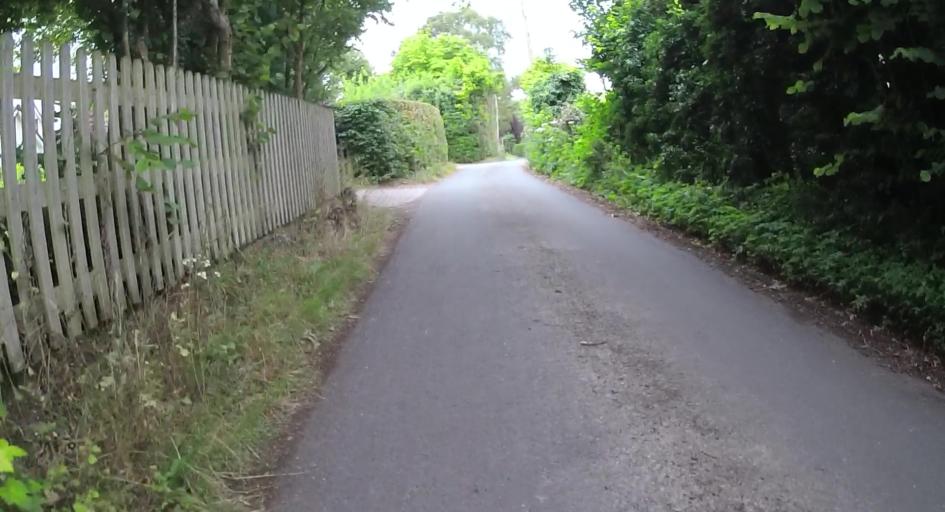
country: GB
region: England
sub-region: Hampshire
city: Four Marks
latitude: 51.0955
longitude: -1.1208
